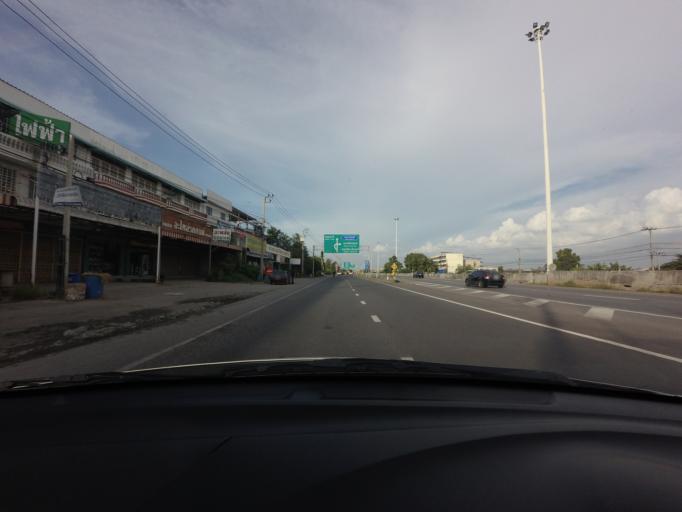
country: TH
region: Nonthaburi
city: Bang Bua Thong
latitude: 13.9498
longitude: 100.4527
